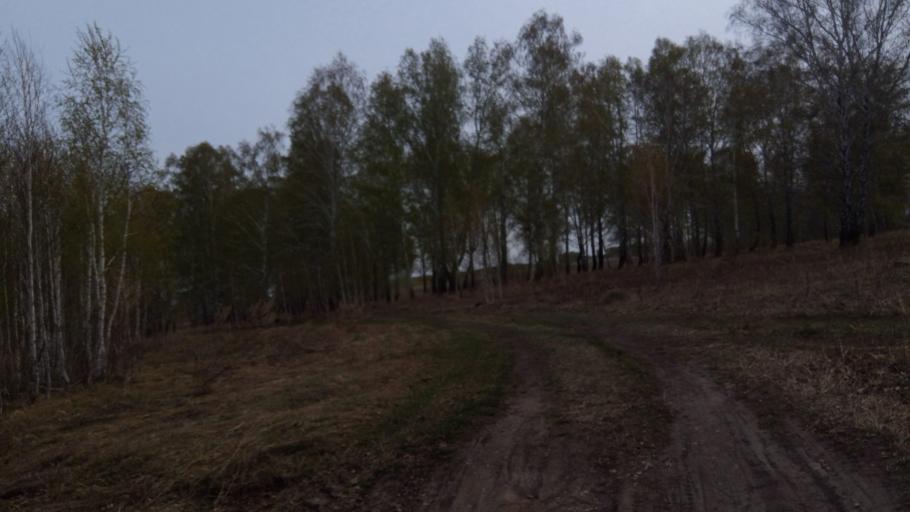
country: RU
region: Chelyabinsk
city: Timiryazevskiy
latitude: 55.0050
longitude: 60.8579
